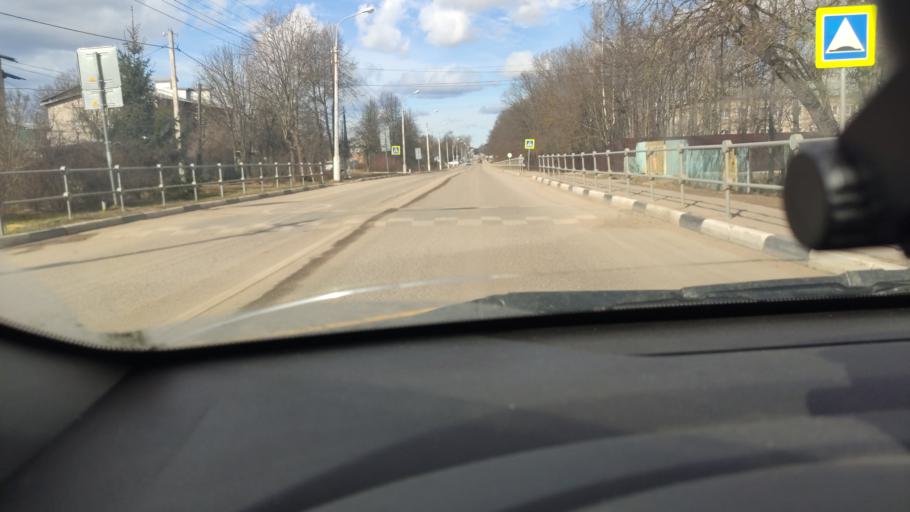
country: RU
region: Moskovskaya
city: Ruza
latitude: 55.7057
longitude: 36.1872
